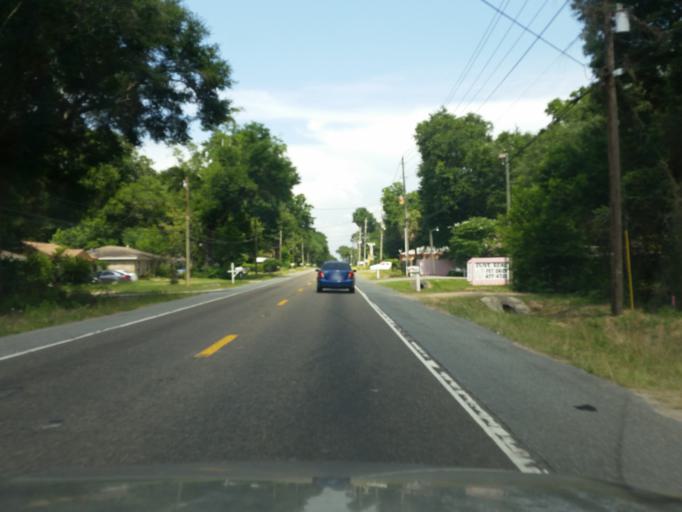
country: US
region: Florida
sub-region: Escambia County
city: Ferry Pass
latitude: 30.5100
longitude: -87.2041
